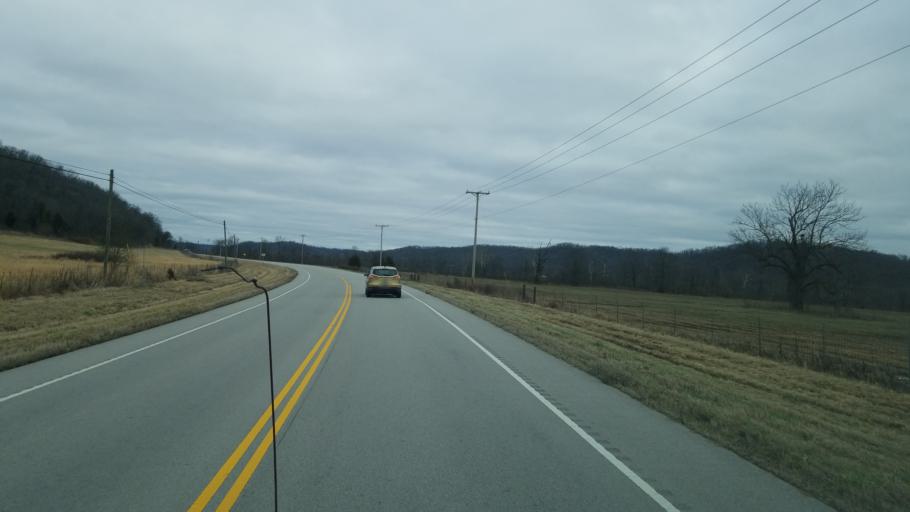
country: US
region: Ohio
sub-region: Adams County
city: Manchester
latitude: 38.6399
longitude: -83.6482
